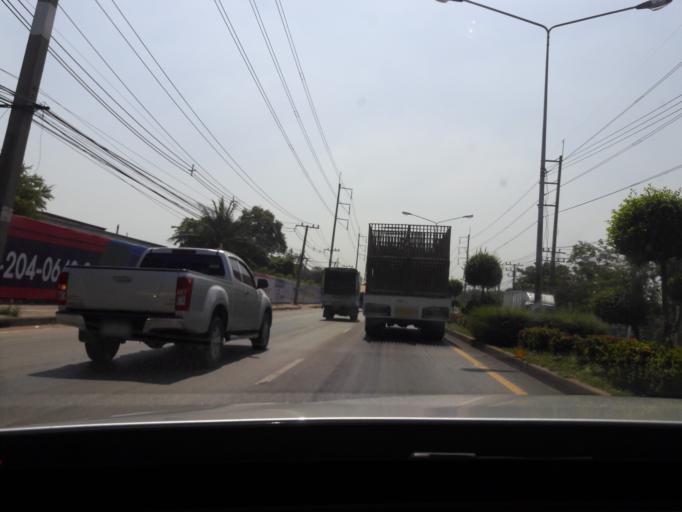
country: TH
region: Samut Sakhon
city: Samut Sakhon
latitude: 13.6015
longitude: 100.2844
